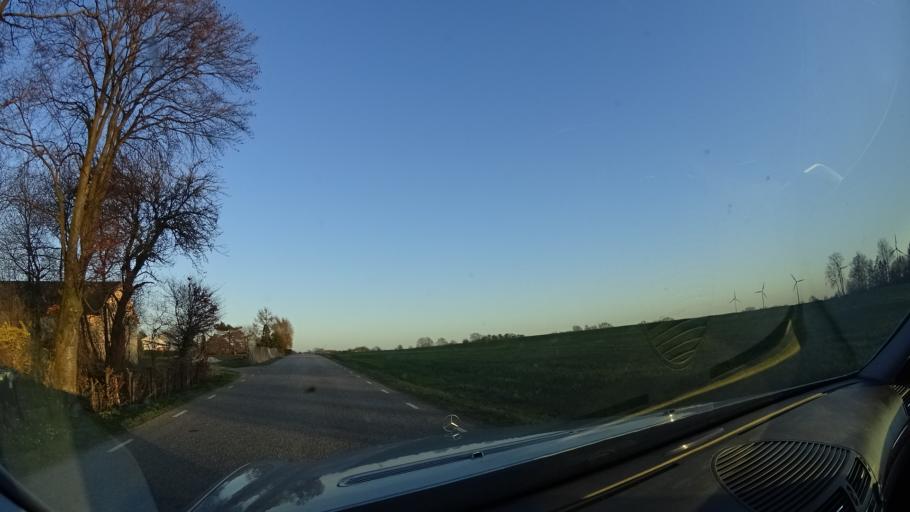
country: SE
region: Skane
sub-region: Hoors Kommun
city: Loberod
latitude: 55.8446
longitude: 13.4505
